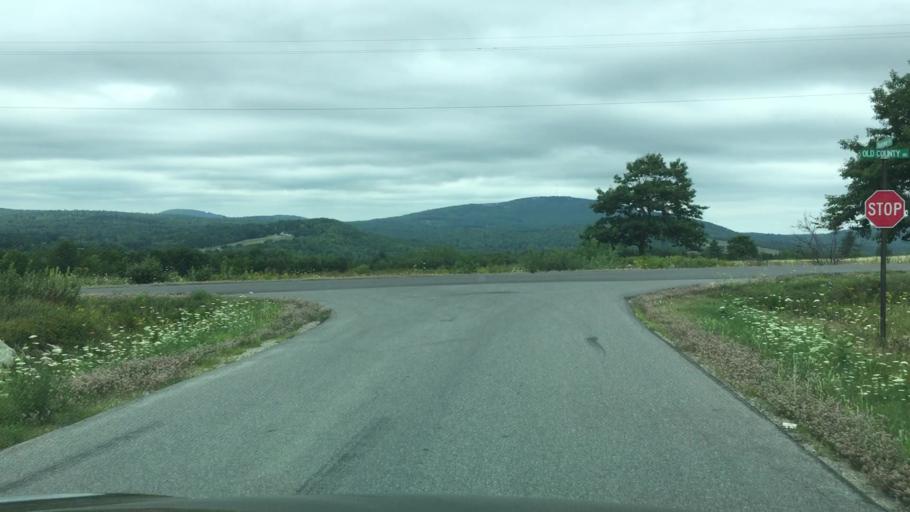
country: US
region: Maine
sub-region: Waldo County
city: Stockton Springs
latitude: 44.5253
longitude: -68.8820
